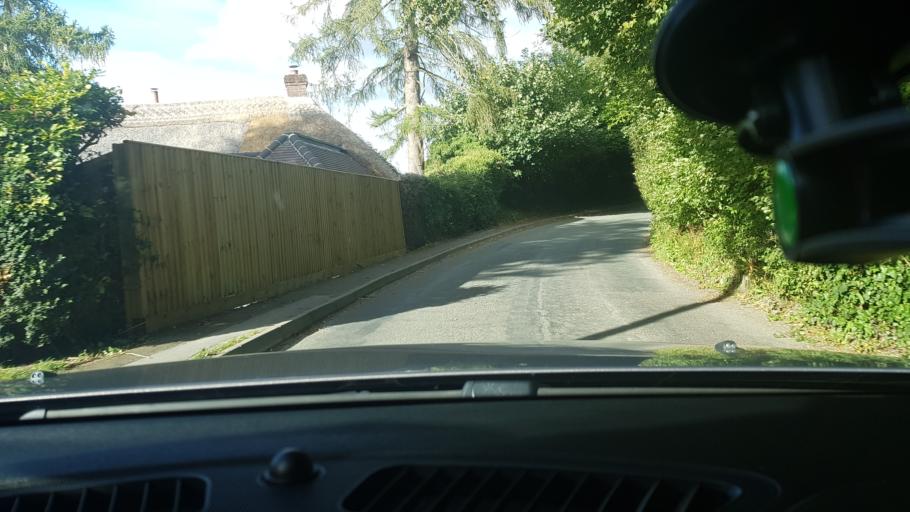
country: GB
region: England
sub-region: Wiltshire
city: Shalbourne
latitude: 51.3664
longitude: -1.5503
